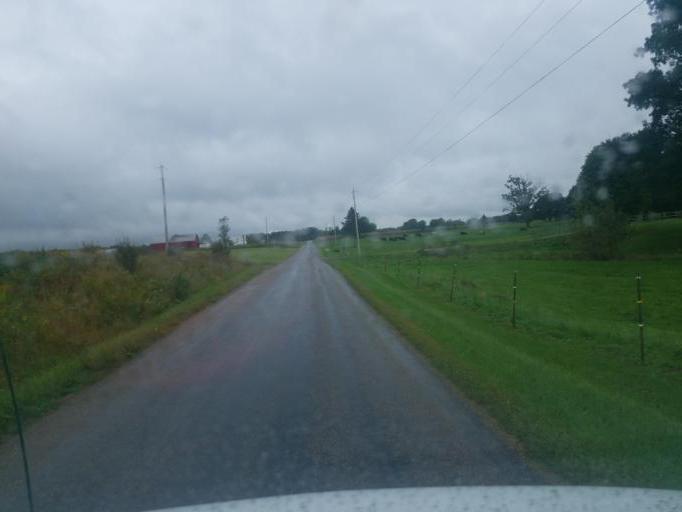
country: US
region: Ohio
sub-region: Wayne County
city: West Salem
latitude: 40.9235
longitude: -82.1187
